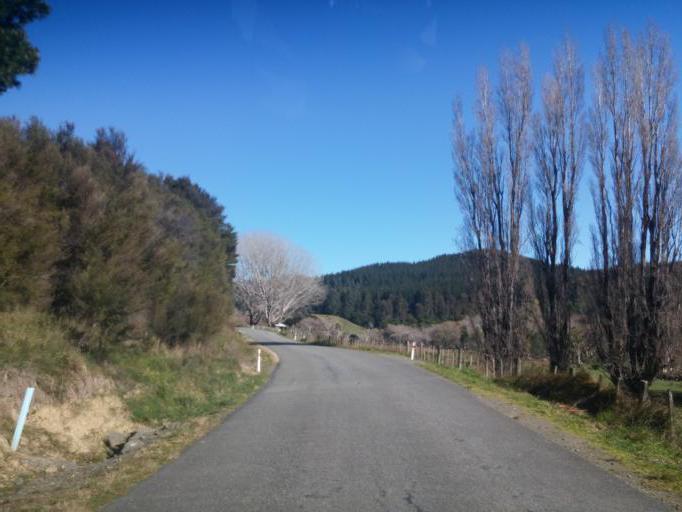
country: NZ
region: Wellington
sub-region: South Wairarapa District
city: Waipawa
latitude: -41.3976
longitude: 175.5022
